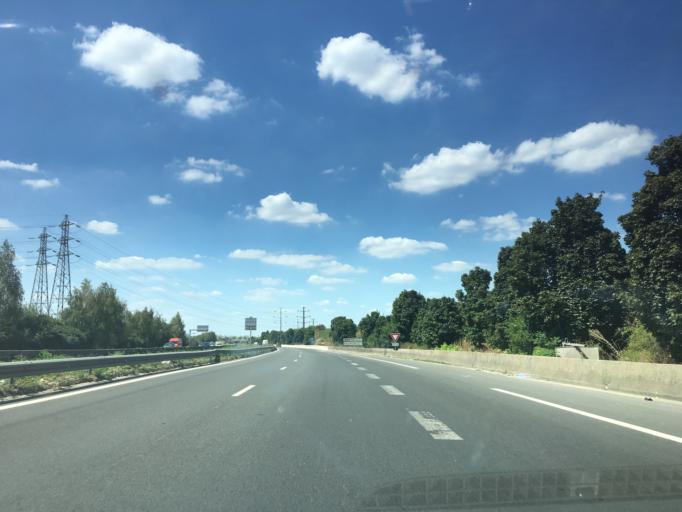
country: FR
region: Ile-de-France
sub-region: Departement du Val-de-Marne
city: Bonneuil-sur-Marne
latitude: 48.7639
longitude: 2.4645
